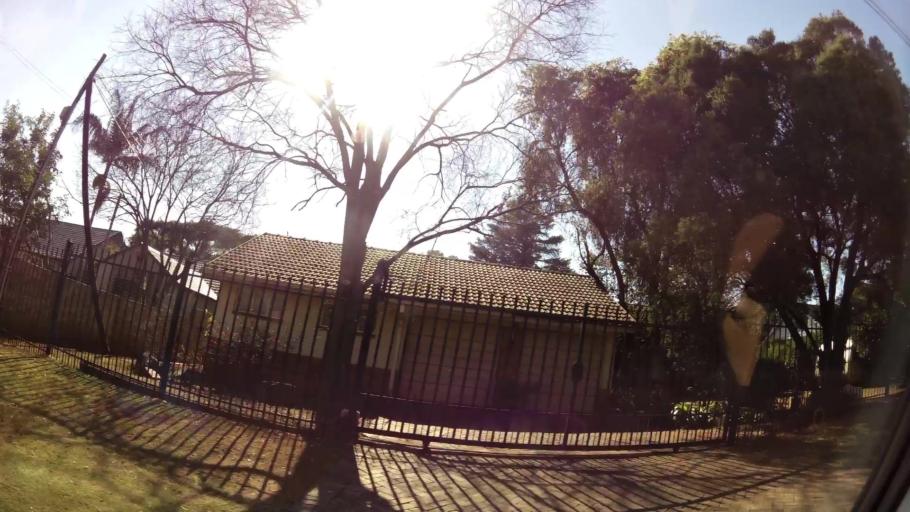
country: ZA
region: Gauteng
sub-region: City of Tshwane Metropolitan Municipality
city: Pretoria
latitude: -25.7616
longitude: 28.2578
